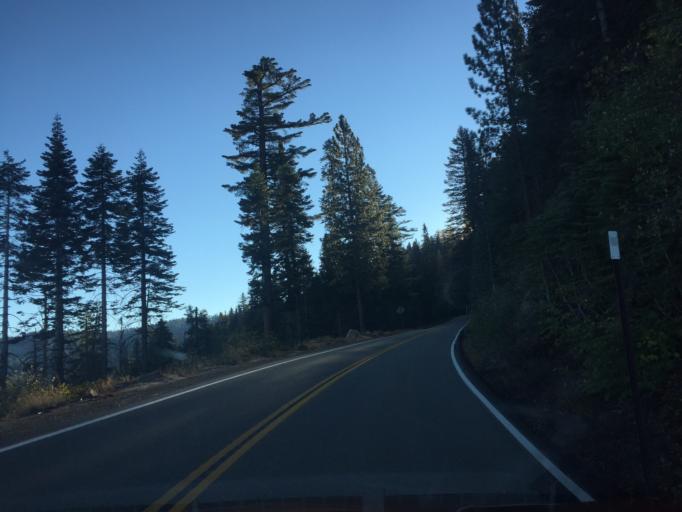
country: US
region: California
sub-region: Mariposa County
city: Yosemite Valley
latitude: 37.6745
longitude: -119.6994
